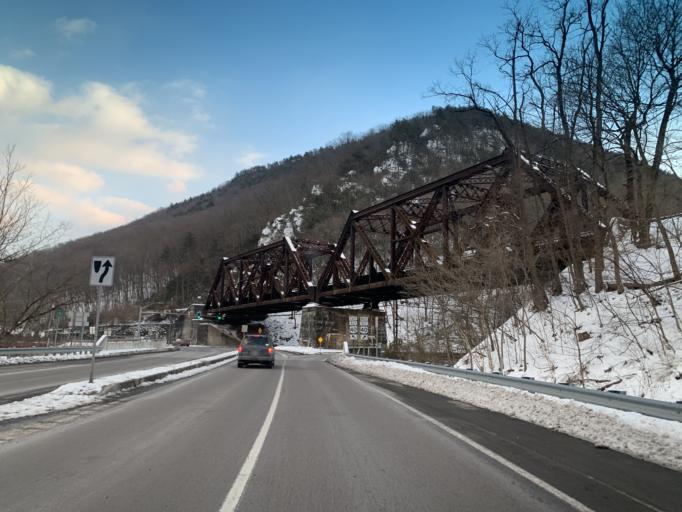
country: US
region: Maryland
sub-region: Allegany County
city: La Vale
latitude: 39.6710
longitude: -78.7910
